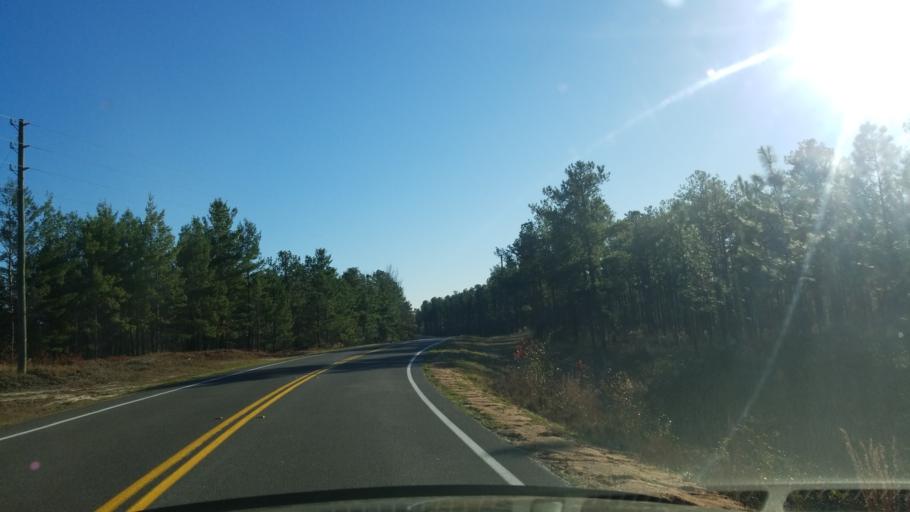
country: US
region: Georgia
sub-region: Talbot County
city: Talbotton
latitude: 32.5738
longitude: -84.5412
